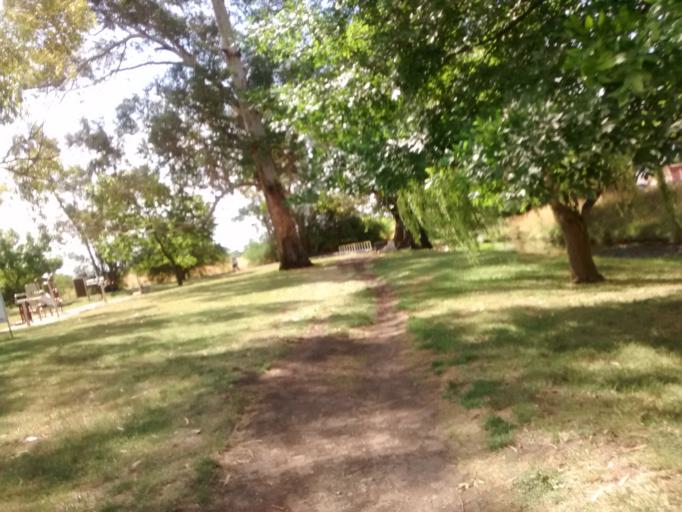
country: AR
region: Buenos Aires
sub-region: Partido de Loberia
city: Loberia
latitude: -38.1779
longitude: -58.7667
